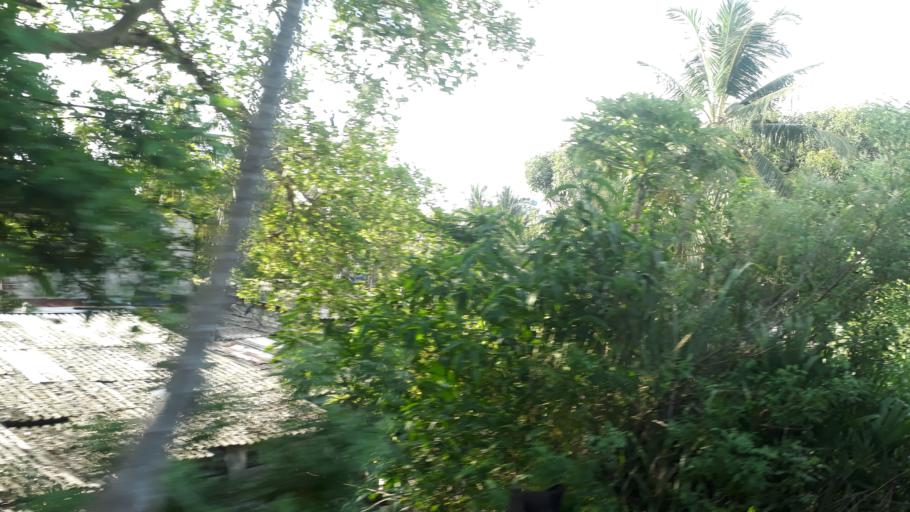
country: LK
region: Western
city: Kolonnawa
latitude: 6.9399
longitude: 79.8817
